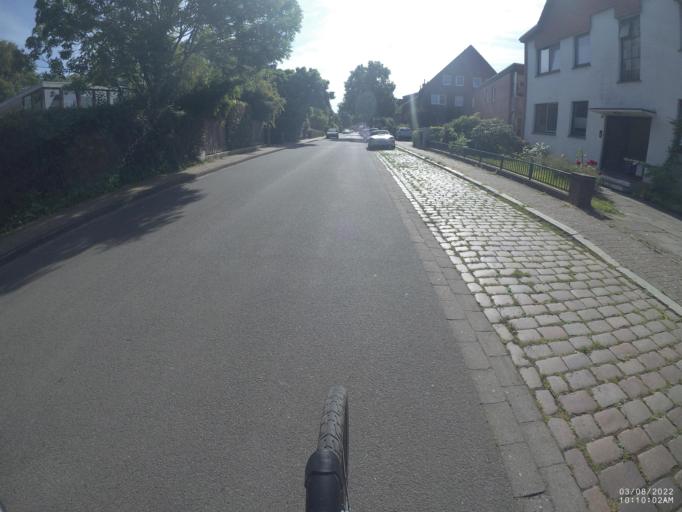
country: DE
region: Lower Saxony
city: Oldenburg
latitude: 53.1432
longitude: 8.1872
